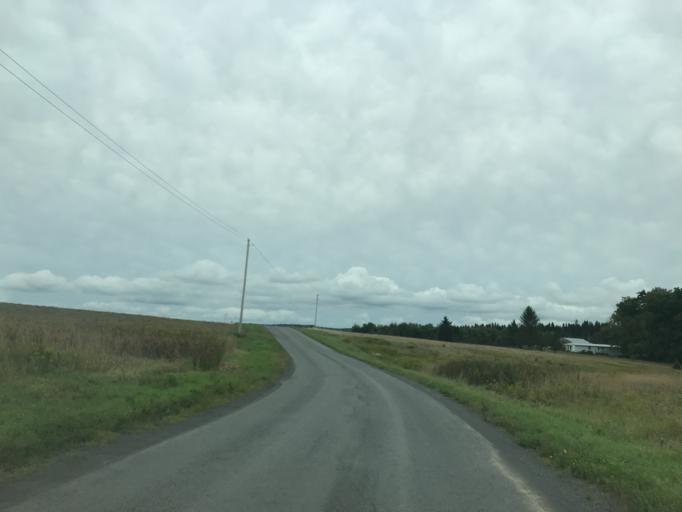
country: US
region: New York
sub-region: Otsego County
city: Worcester
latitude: 42.5363
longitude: -74.6457
